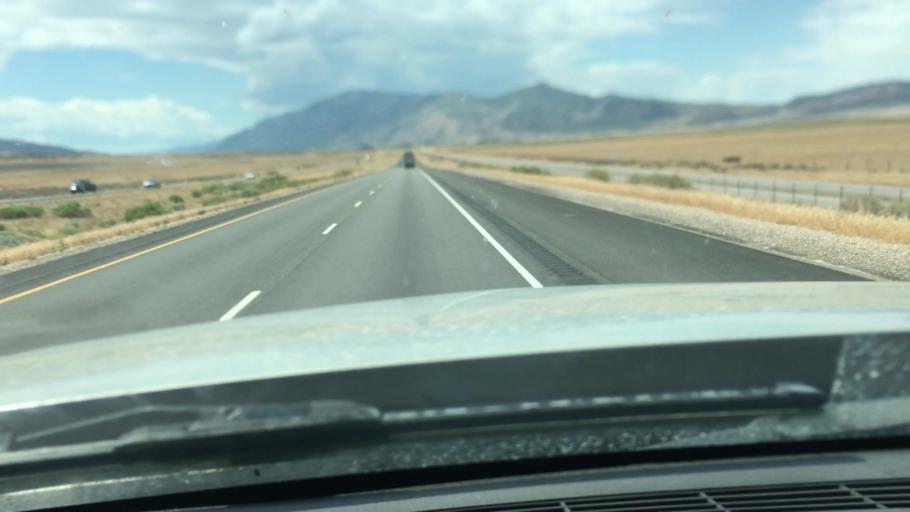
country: US
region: Utah
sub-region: Sanpete County
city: Gunnison
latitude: 39.3018
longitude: -112.0891
